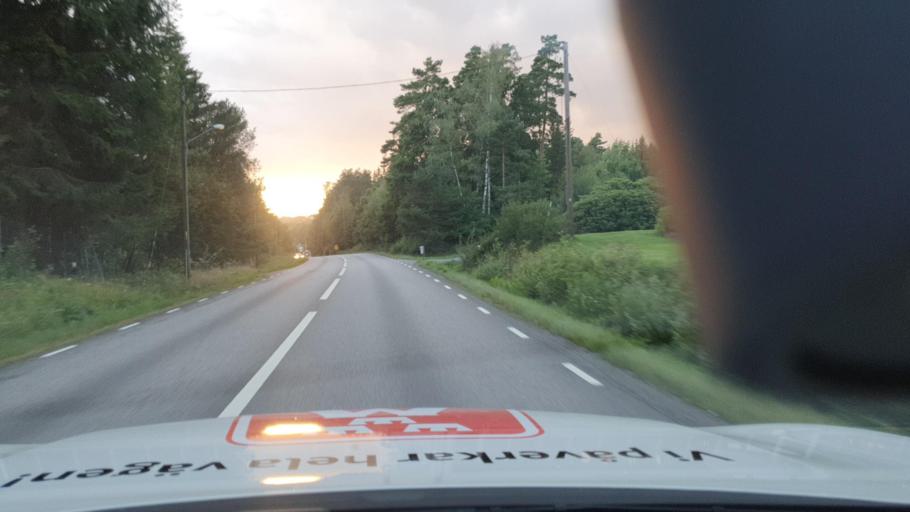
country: SE
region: Vaestra Goetaland
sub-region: Marks Kommun
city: Kinna
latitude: 57.4720
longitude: 12.7259
